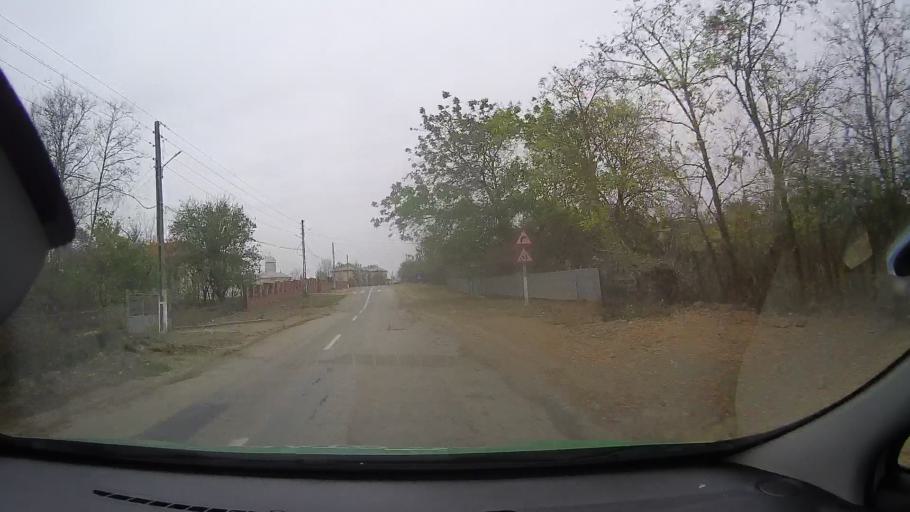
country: RO
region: Constanta
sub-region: Comuna Vulturu
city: Vulturu
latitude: 44.6464
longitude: 28.2705
